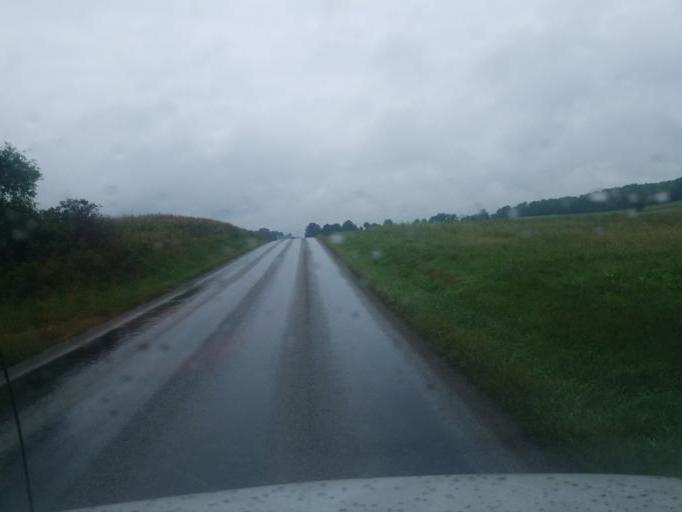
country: US
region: Ohio
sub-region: Wayne County
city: Creston
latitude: 40.9744
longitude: -81.9326
